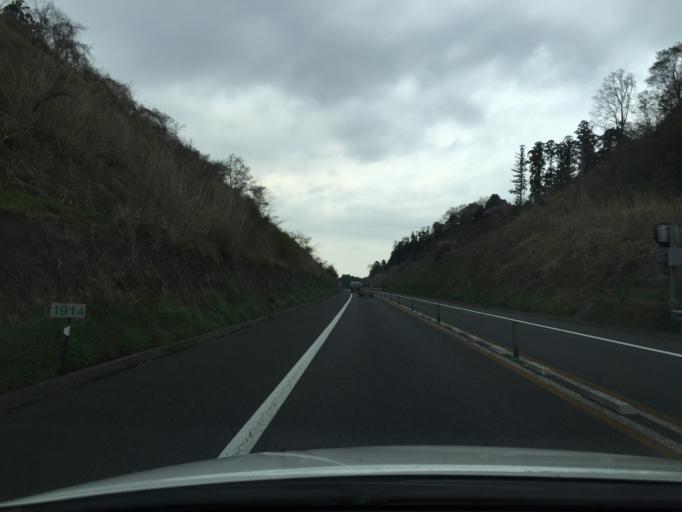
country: JP
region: Fukushima
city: Iwaki
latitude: 37.1488
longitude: 140.9653
